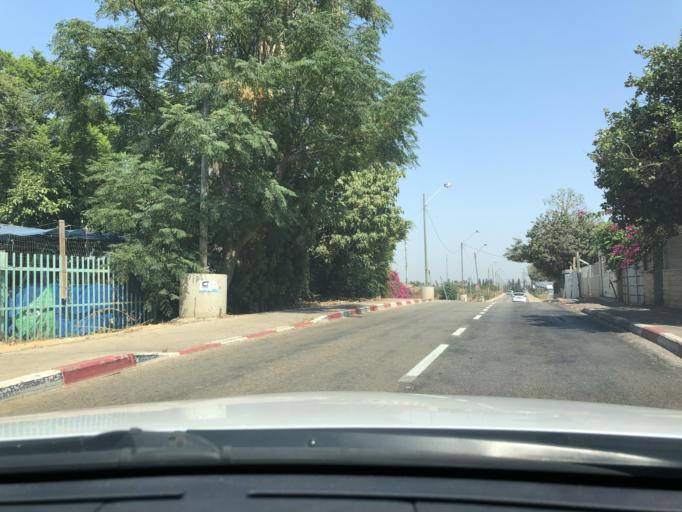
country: IL
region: Central District
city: Kfar Saba
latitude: 32.1650
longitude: 34.9119
